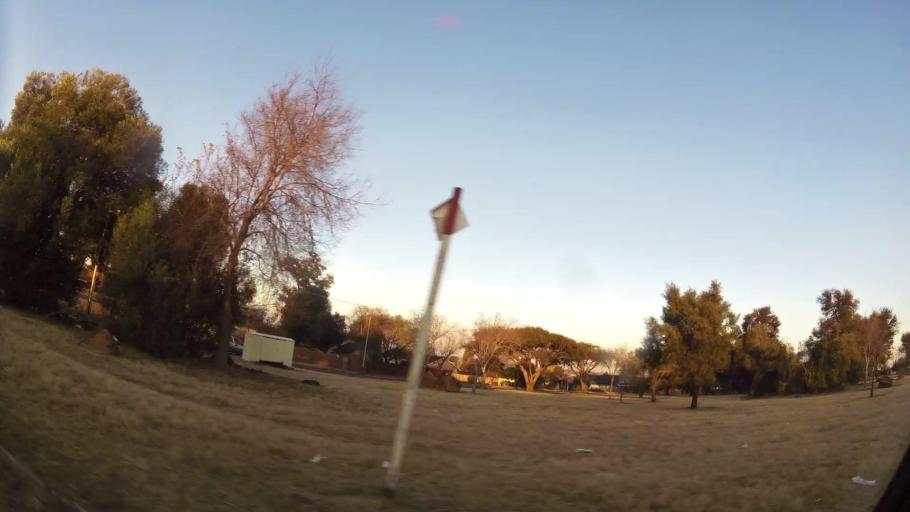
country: ZA
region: Gauteng
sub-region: Ekurhuleni Metropolitan Municipality
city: Germiston
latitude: -26.2590
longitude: 28.1635
